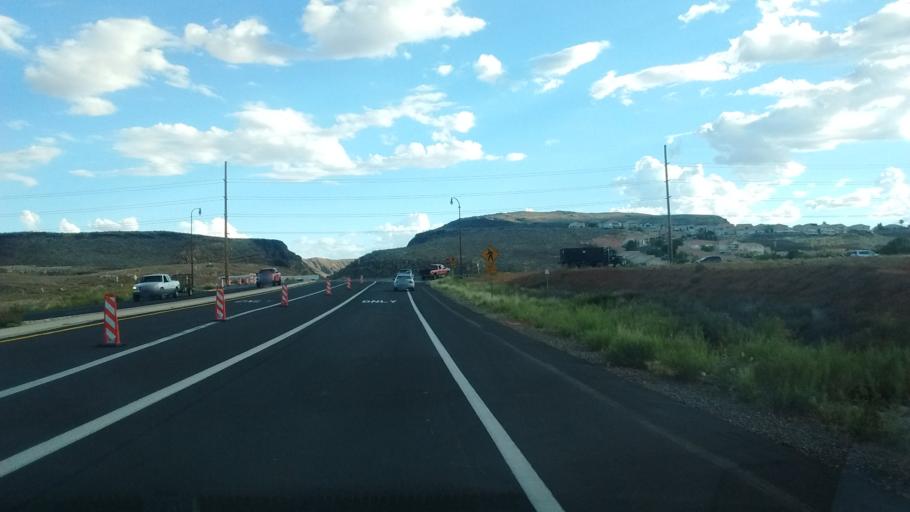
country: US
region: Utah
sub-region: Washington County
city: Washington
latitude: 37.1325
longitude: -113.4856
